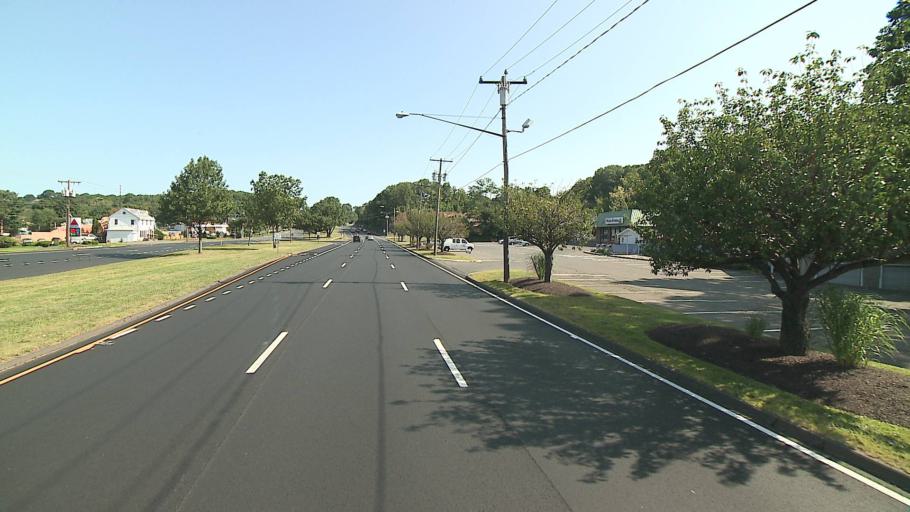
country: US
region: Connecticut
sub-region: Hartford County
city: Newington
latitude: 41.6853
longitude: -72.7086
